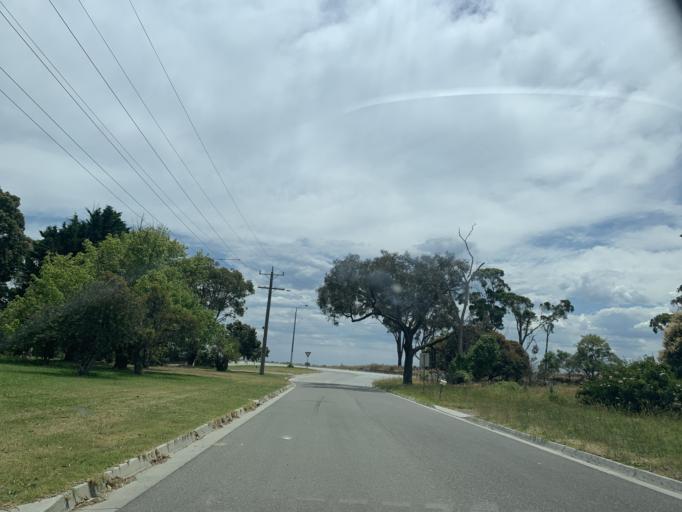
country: AU
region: Victoria
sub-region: Casey
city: Cranbourne South
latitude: -38.1295
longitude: 145.2400
